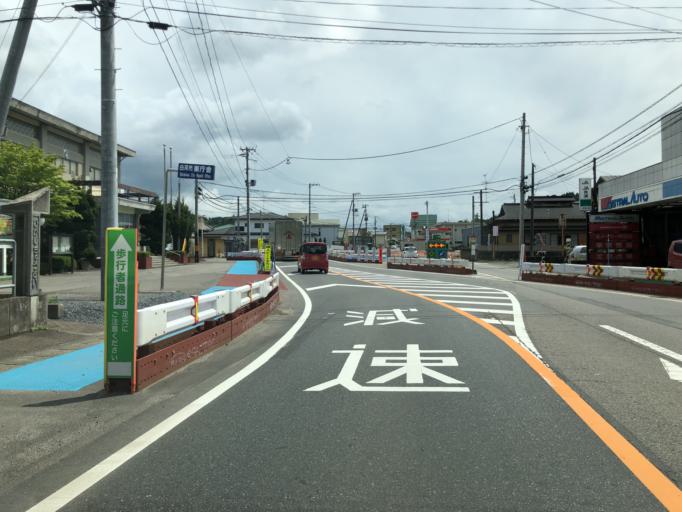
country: JP
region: Fukushima
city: Ishikawa
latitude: 37.1025
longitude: 140.3486
